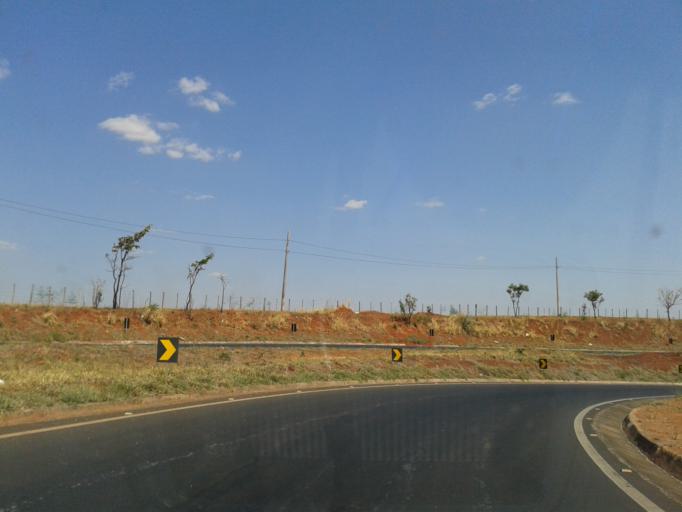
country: BR
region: Minas Gerais
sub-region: Uberlandia
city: Uberlandia
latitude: -18.8587
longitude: -48.2527
